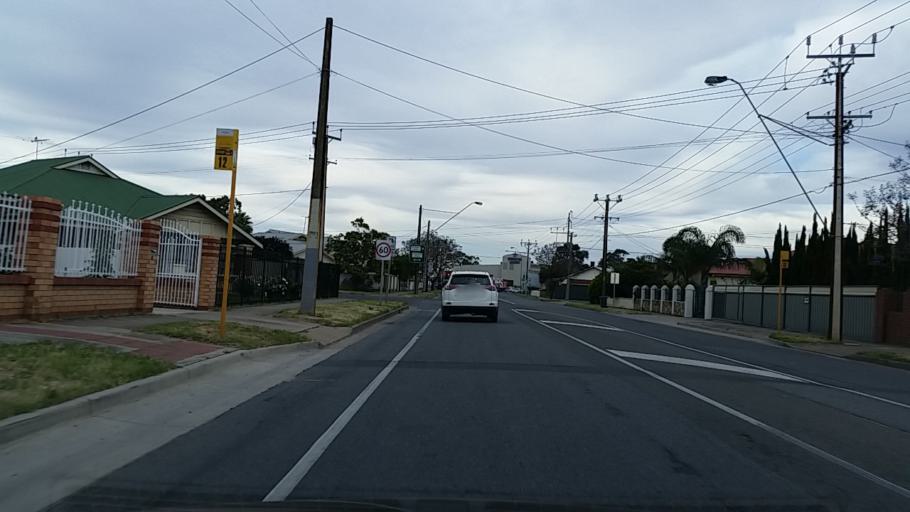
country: AU
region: South Australia
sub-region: Charles Sturt
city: Woodville
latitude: -34.8784
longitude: 138.5504
